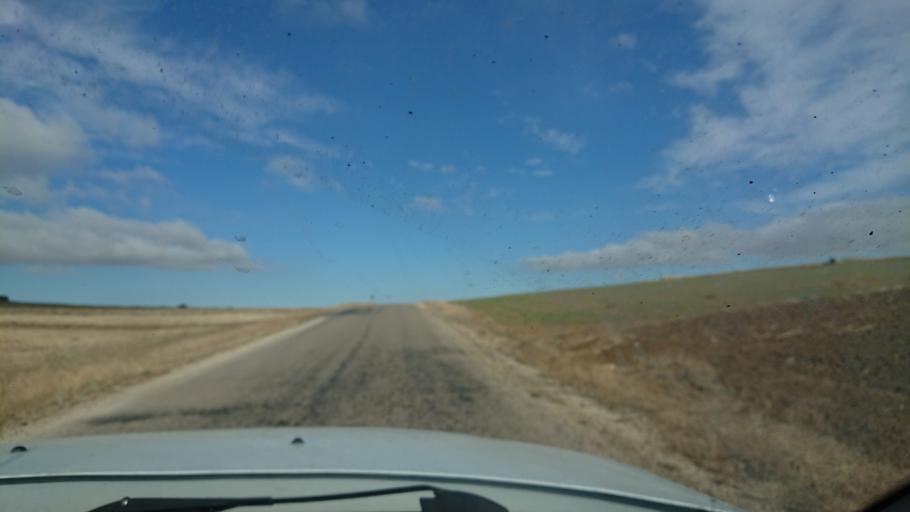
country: TR
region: Aksaray
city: Agacoren
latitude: 38.8370
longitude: 33.9542
